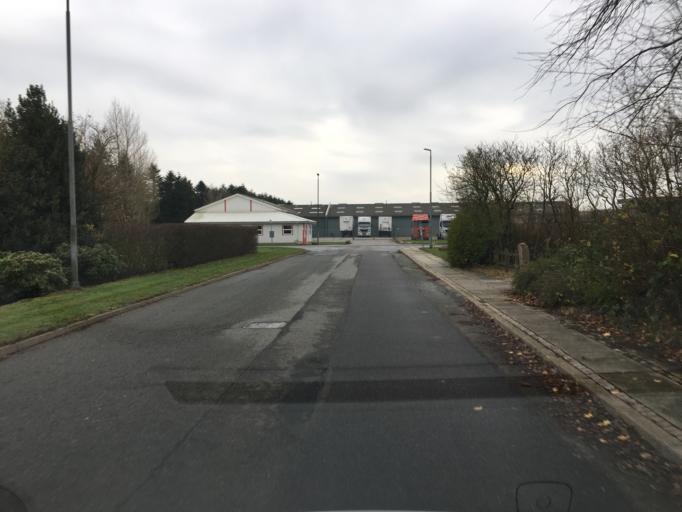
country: DK
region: South Denmark
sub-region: Tonder Kommune
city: Tonder
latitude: 54.9508
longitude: 8.8669
